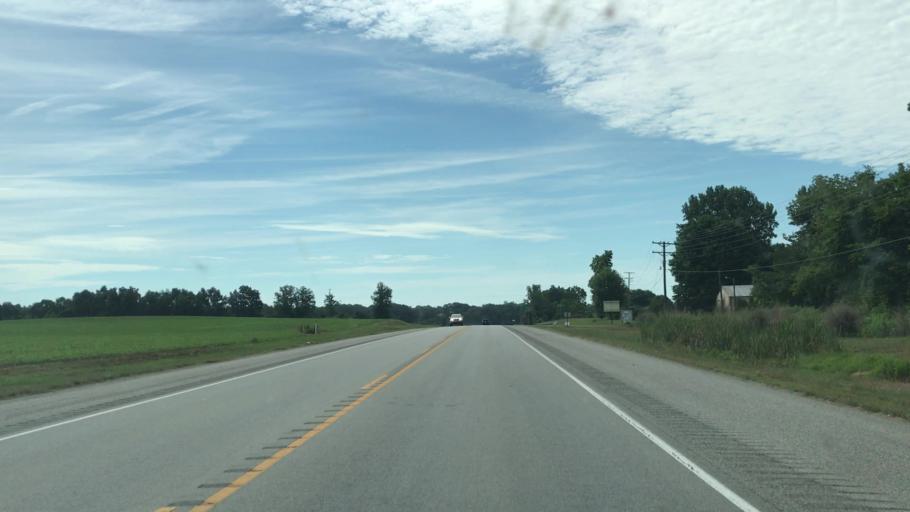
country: US
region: Kentucky
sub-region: Edmonson County
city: Brownsville
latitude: 37.1682
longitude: -86.2299
